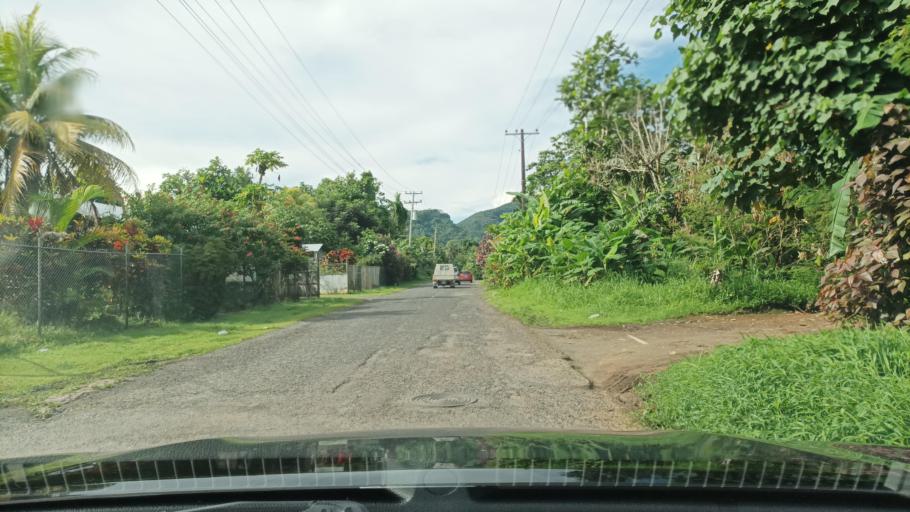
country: FM
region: Pohnpei
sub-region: Kolonia Municipality
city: Kolonia Town
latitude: 6.9453
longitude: 158.1950
